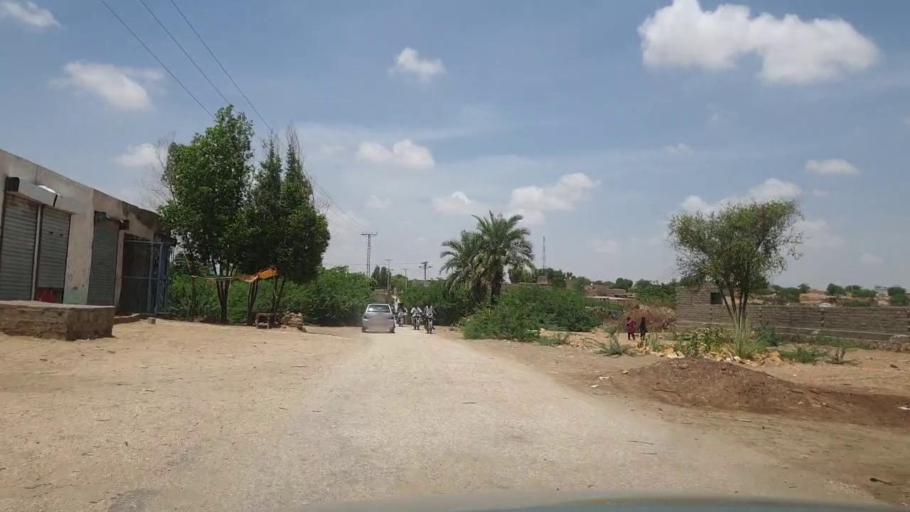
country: PK
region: Sindh
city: Kot Diji
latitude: 27.1592
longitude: 68.9671
